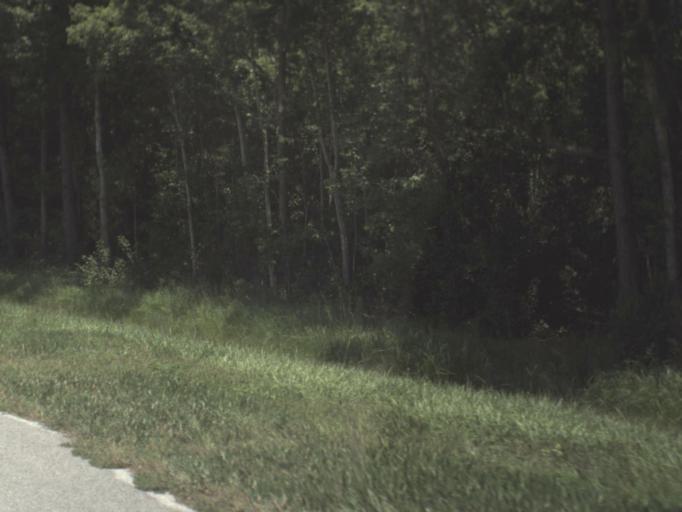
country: US
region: Florida
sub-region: Bradford County
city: Starke
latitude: 30.0177
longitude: -82.1485
